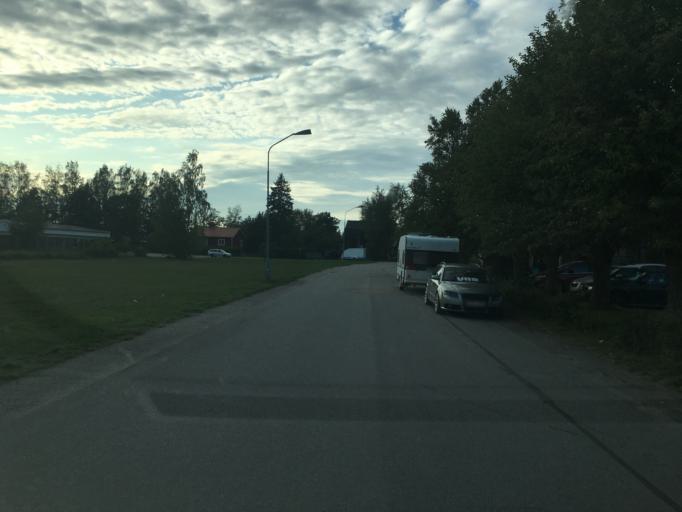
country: SE
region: Vaestmanland
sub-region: Vasteras
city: Tillberga
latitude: 59.6844
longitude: 16.6146
